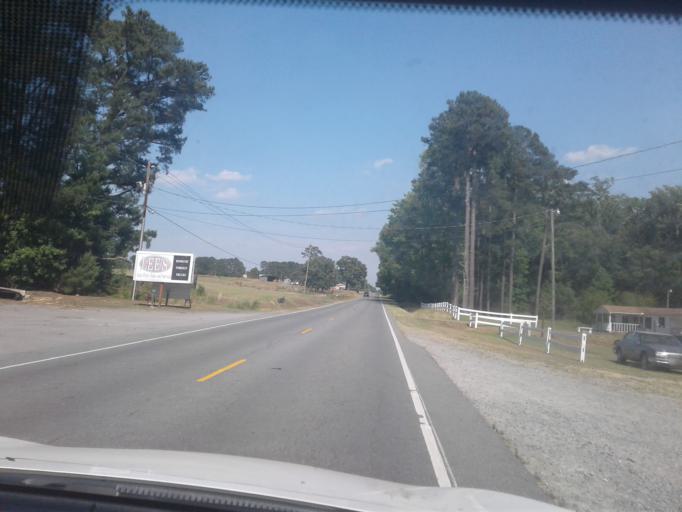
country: US
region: North Carolina
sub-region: Johnston County
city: Benson
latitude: 35.3888
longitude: -78.5729
